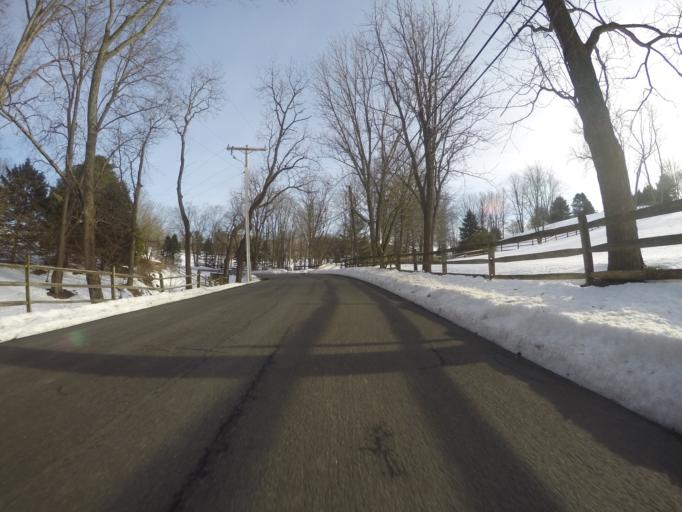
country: US
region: Maryland
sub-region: Baltimore County
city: Hunt Valley
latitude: 39.5581
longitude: -76.6040
